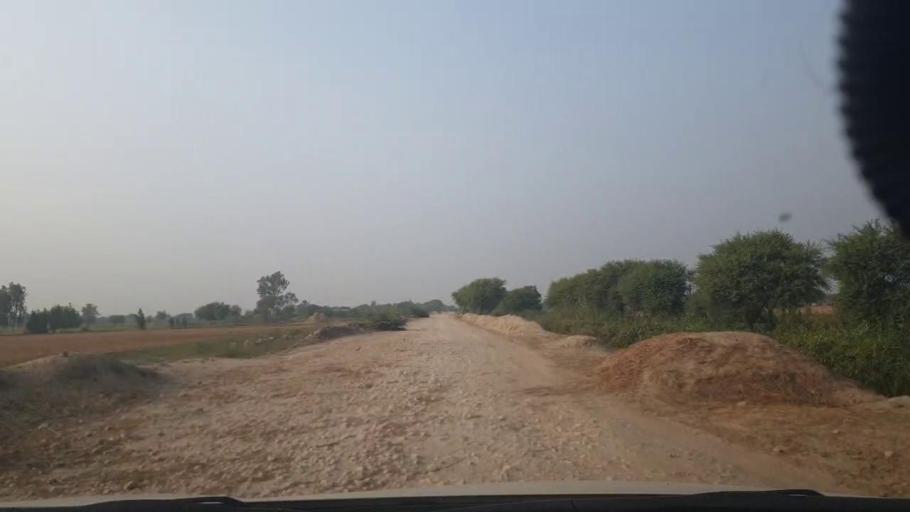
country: PK
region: Sindh
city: Bulri
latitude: 24.7987
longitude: 68.4148
